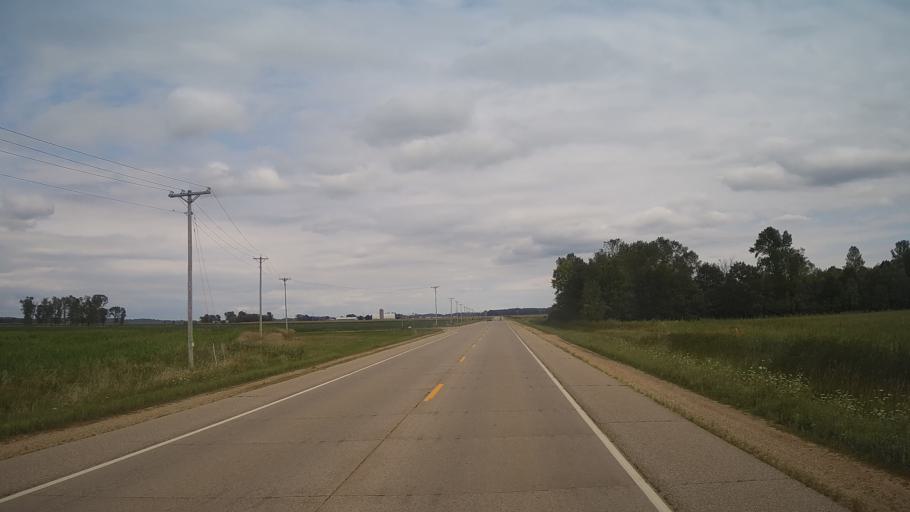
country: US
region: Wisconsin
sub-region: Waushara County
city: Redgranite
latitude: 44.0375
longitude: -89.0635
